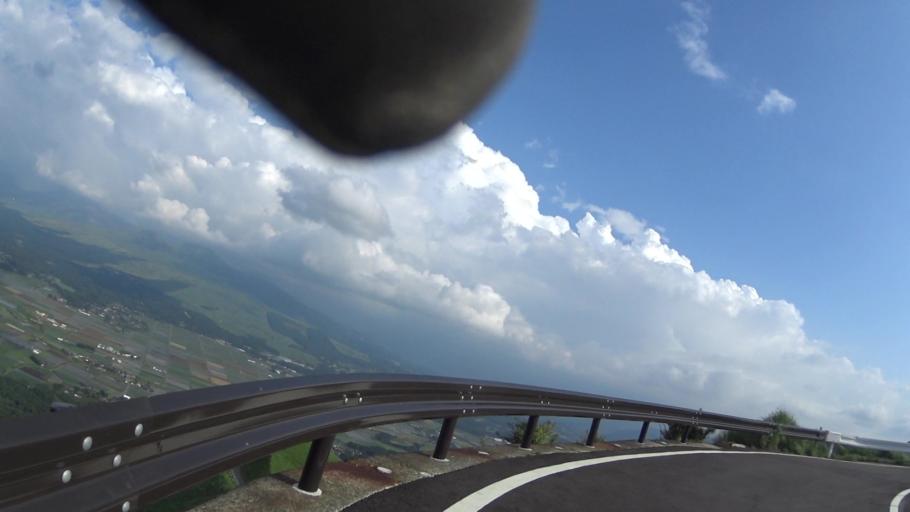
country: JP
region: Kumamoto
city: Aso
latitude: 32.9616
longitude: 131.0016
